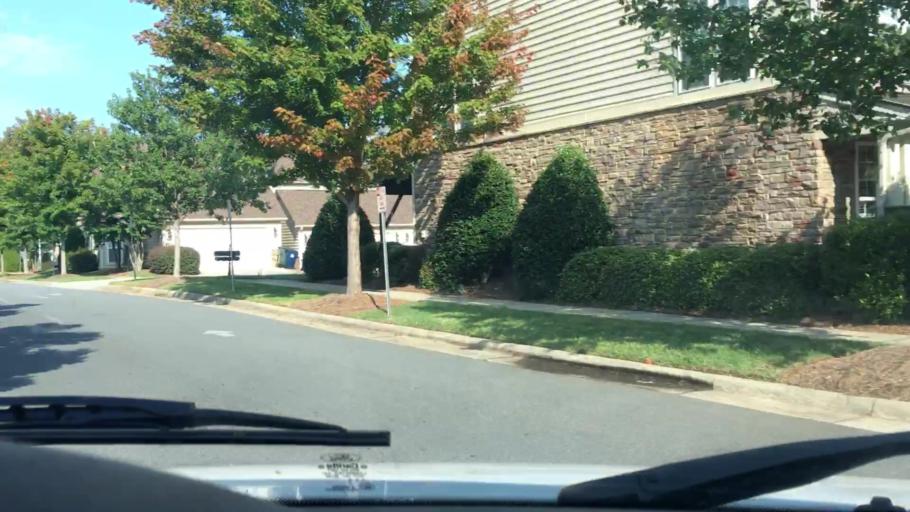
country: US
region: North Carolina
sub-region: Mecklenburg County
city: Cornelius
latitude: 35.4651
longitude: -80.8866
